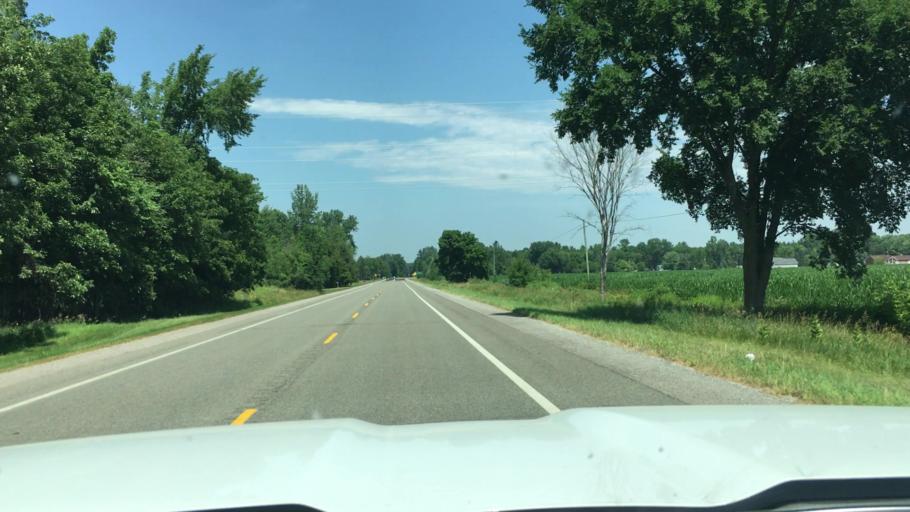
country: US
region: Michigan
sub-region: Saginaw County
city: Chesaning
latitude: 43.2104
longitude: -84.1694
